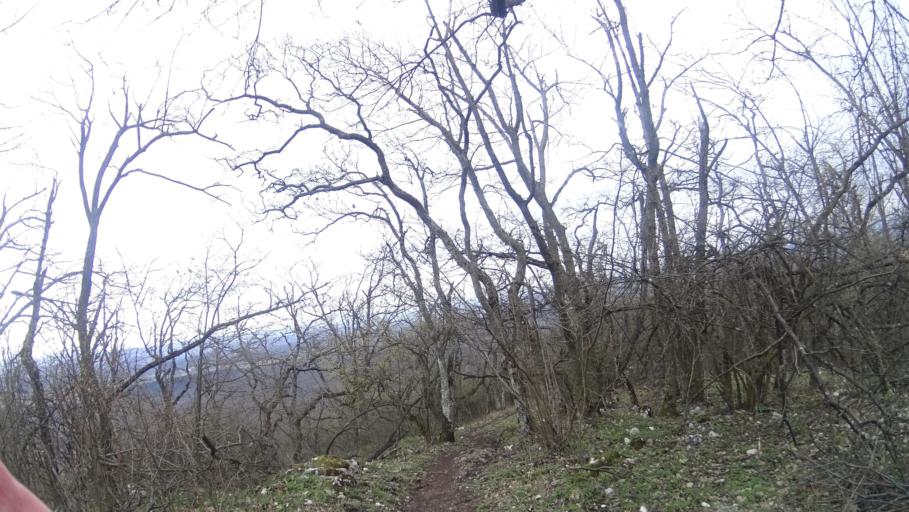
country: HU
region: Pest
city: Kosd
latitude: 47.8342
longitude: 19.1577
